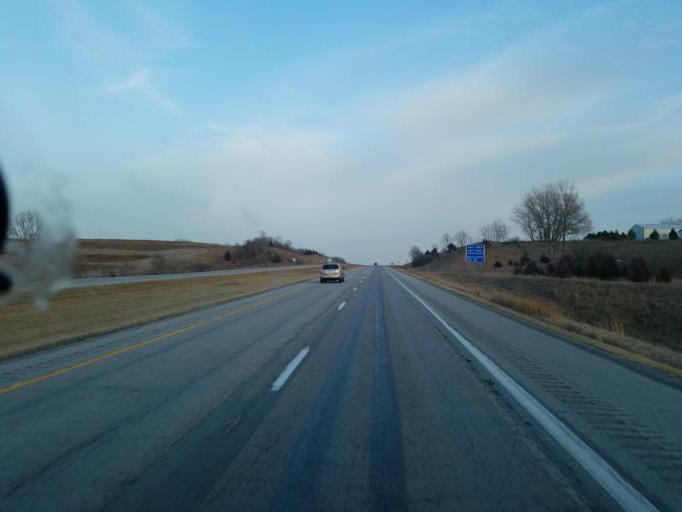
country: US
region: Iowa
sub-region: Harrison County
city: Missouri Valley
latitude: 41.4933
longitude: -95.8515
